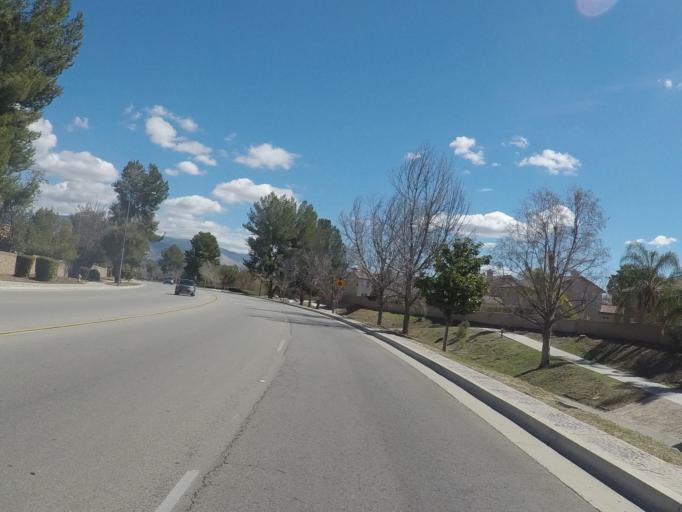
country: US
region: California
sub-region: Riverside County
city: San Jacinto
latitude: 33.7695
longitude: -116.9378
